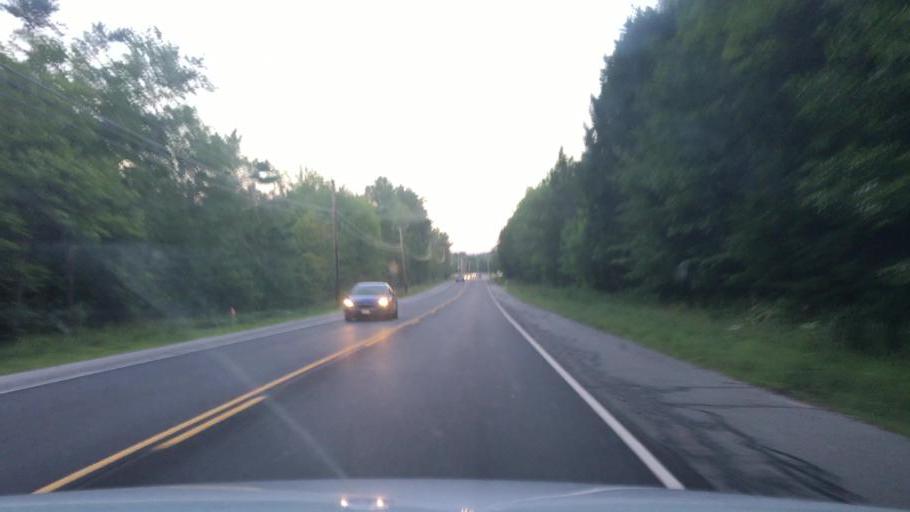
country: US
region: Maine
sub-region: Androscoggin County
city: Turner
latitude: 44.2381
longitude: -70.2583
